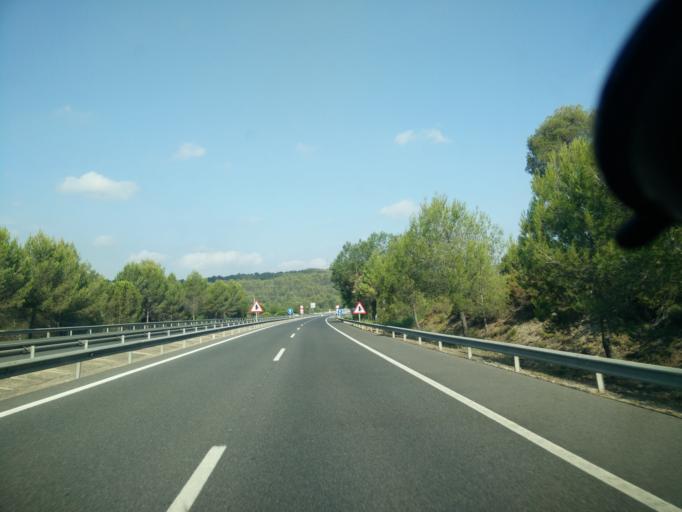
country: ES
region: Catalonia
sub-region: Provincia de Barcelona
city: Rubi
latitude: 41.5149
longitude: 2.0407
